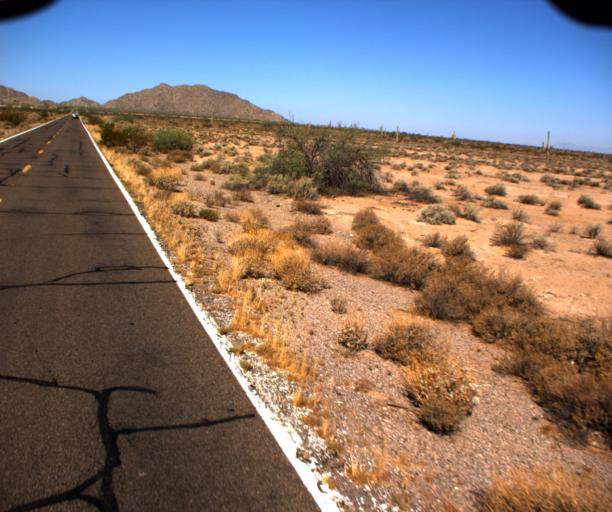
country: US
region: Arizona
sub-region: Pinal County
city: Sacaton
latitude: 33.0552
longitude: -111.6999
